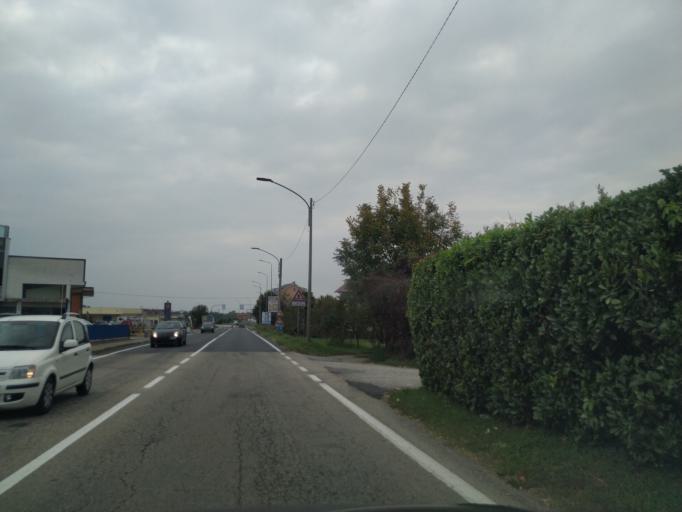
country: IT
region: Piedmont
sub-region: Provincia di Torino
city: Chivasso
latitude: 45.1901
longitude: 7.8721
